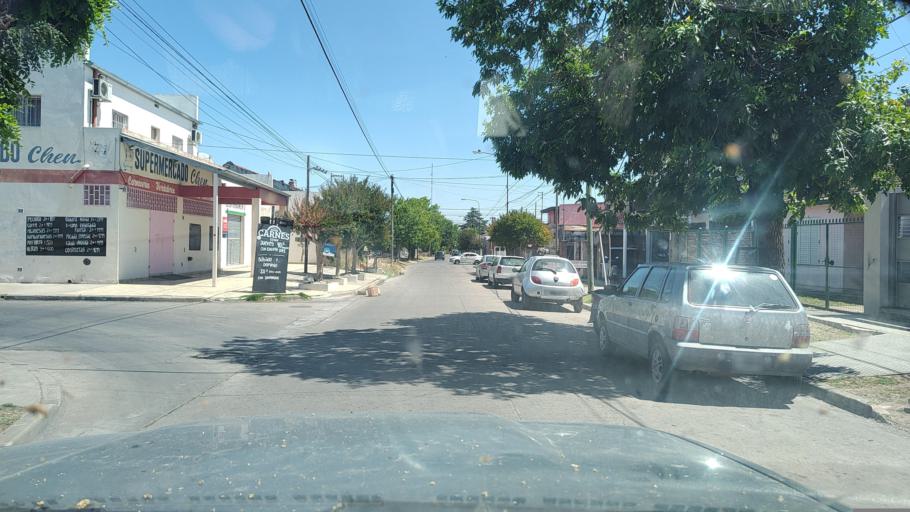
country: AR
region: Buenos Aires
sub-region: Partido de Lujan
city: Lujan
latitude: -34.5818
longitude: -59.1109
